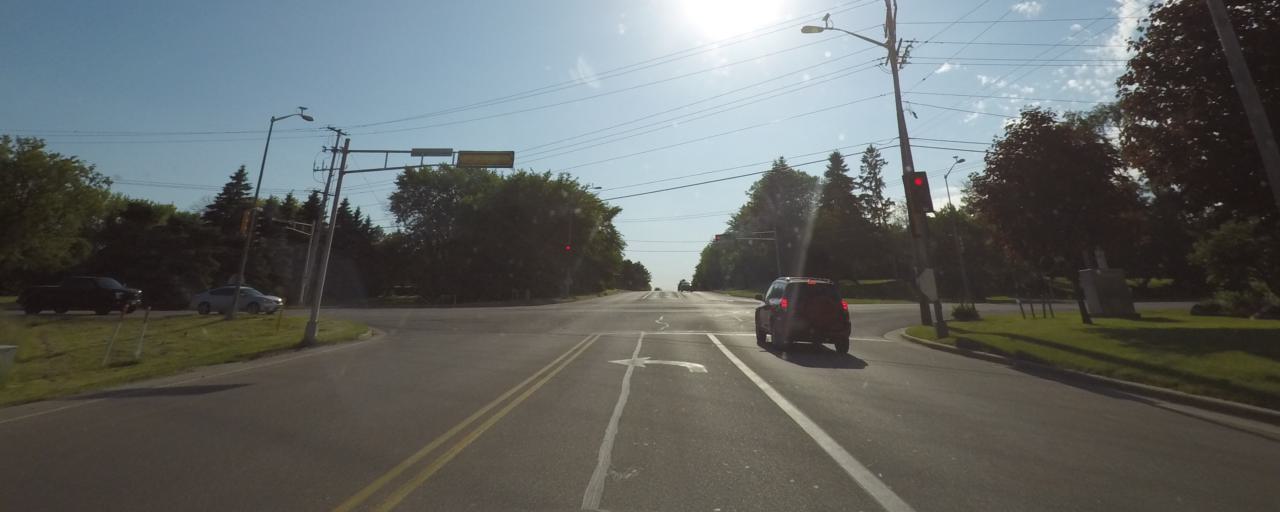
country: US
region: Wisconsin
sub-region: Waukesha County
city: New Berlin
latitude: 42.9552
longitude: -88.0887
